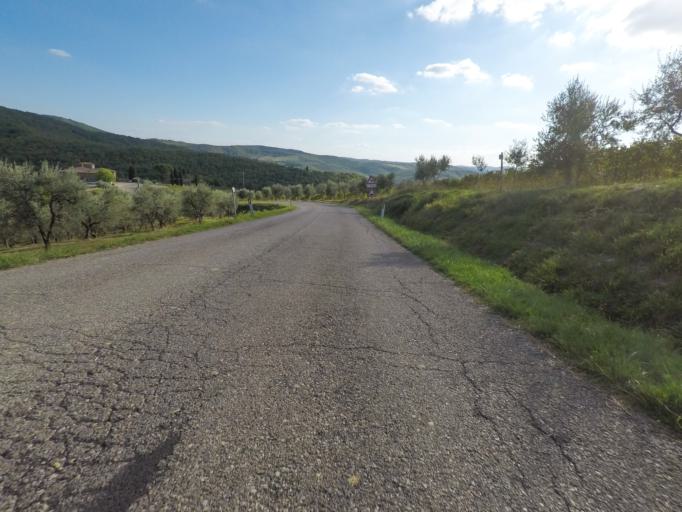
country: IT
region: Tuscany
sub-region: Provincia di Siena
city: Radda in Chianti
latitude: 43.5155
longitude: 11.4063
